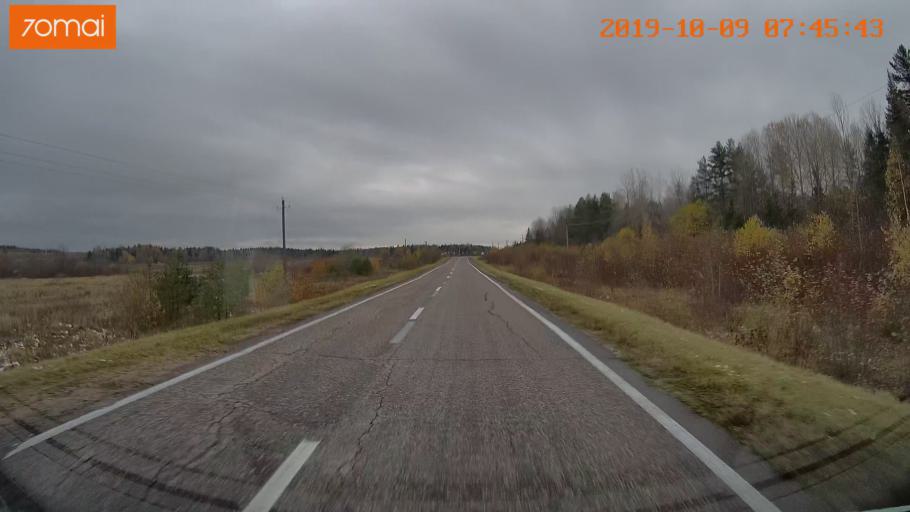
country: RU
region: Jaroslavl
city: Kukoboy
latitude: 58.6550
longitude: 39.7729
